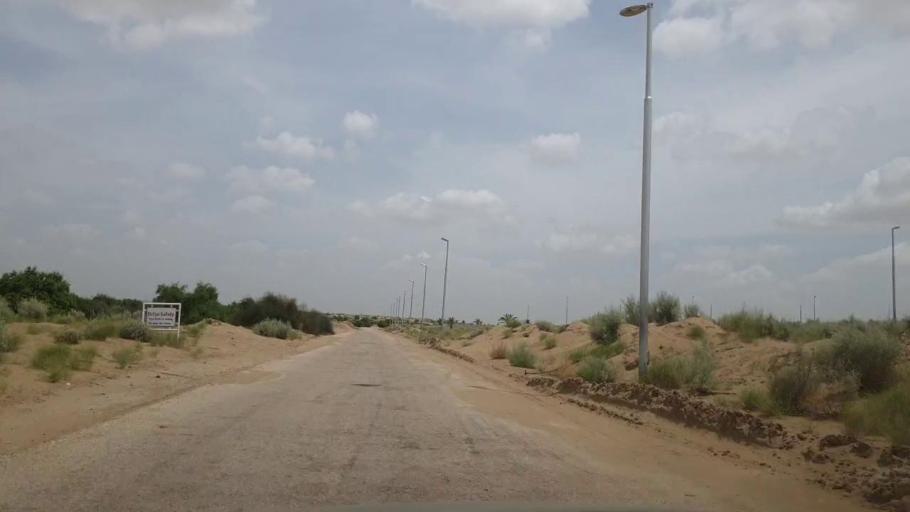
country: PK
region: Sindh
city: Kot Diji
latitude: 27.1949
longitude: 69.1618
